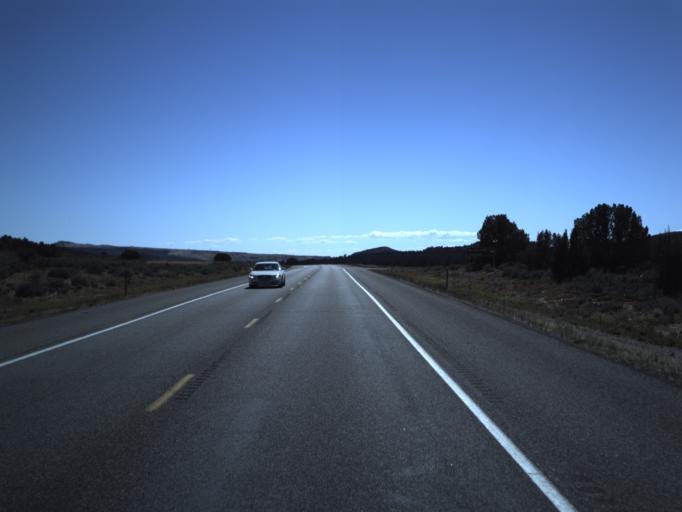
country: US
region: Utah
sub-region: Washington County
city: Ivins
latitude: 37.2811
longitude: -113.6532
